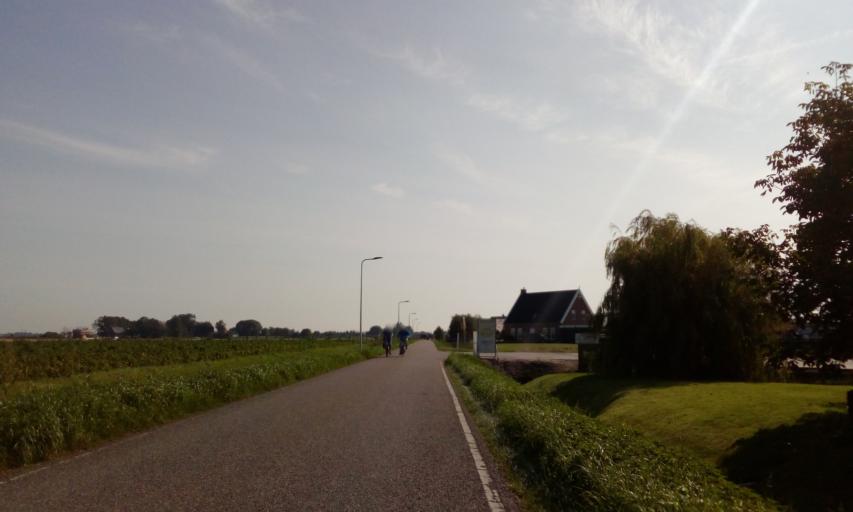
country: NL
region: South Holland
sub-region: Gemeente Waddinxveen
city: Groenswaard
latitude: 52.0456
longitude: 4.6007
